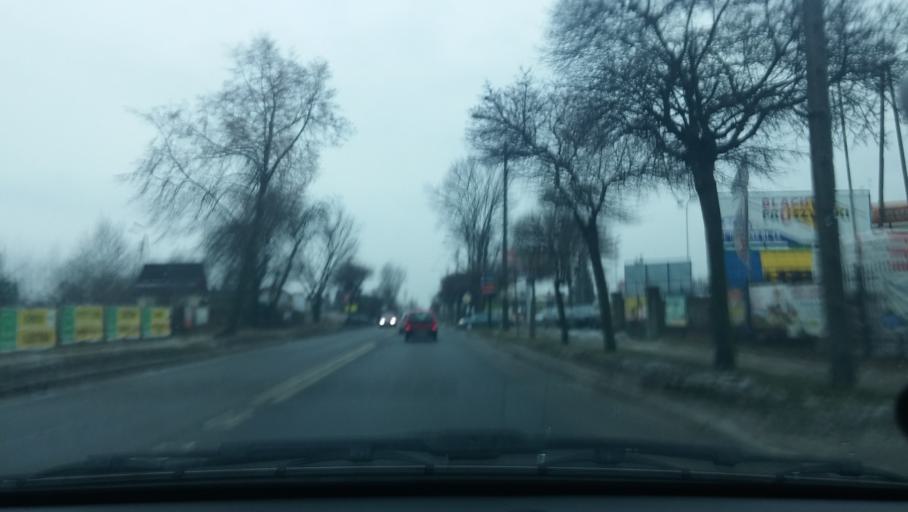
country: PL
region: Masovian Voivodeship
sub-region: Siedlce
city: Siedlce
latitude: 52.1902
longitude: 22.2661
